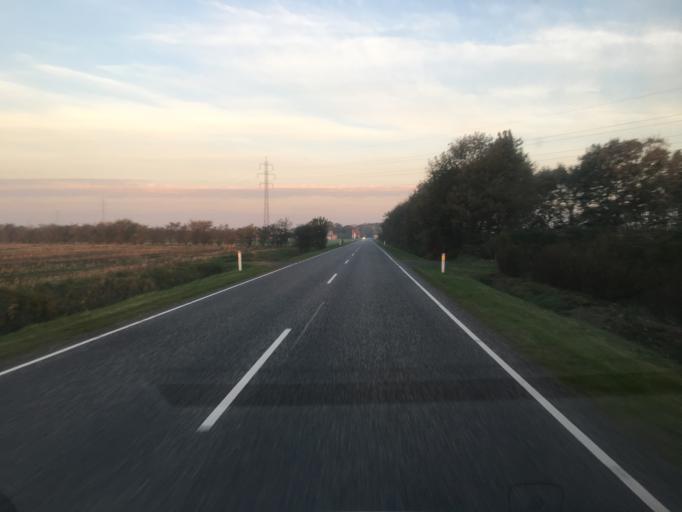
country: DK
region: South Denmark
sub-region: Tonder Kommune
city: Logumkloster
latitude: 55.0369
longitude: 9.0340
